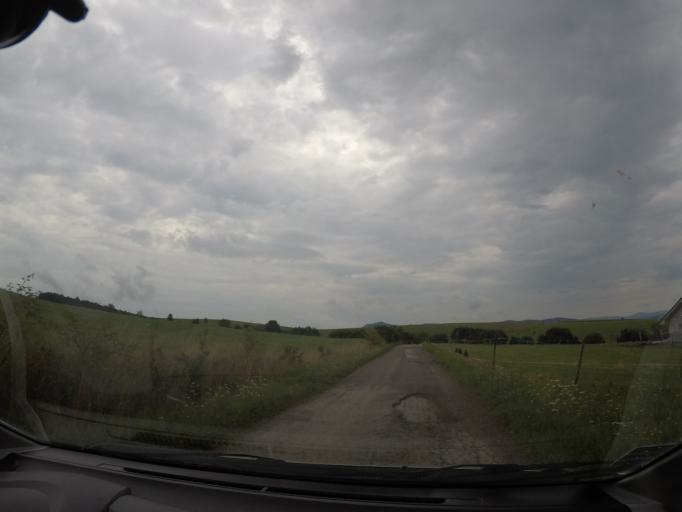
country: SK
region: Nitriansky
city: Bojnice
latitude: 48.9051
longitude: 18.6123
